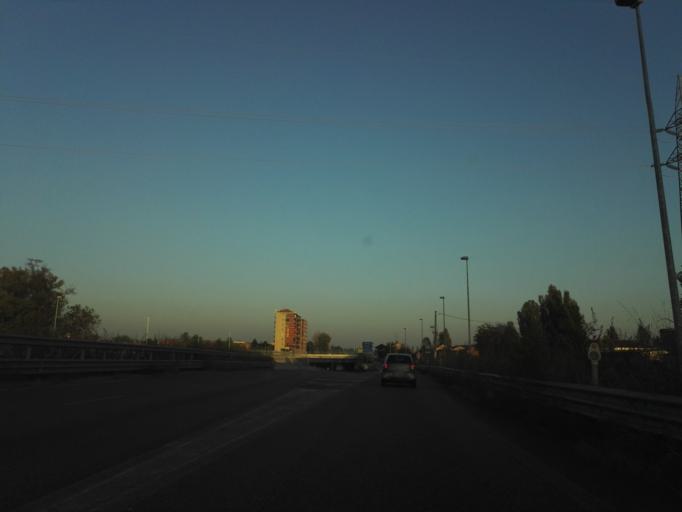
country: IT
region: Lombardy
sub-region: Citta metropolitana di Milano
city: Vigliano-Bettolino
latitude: 45.4297
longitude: 9.3440
